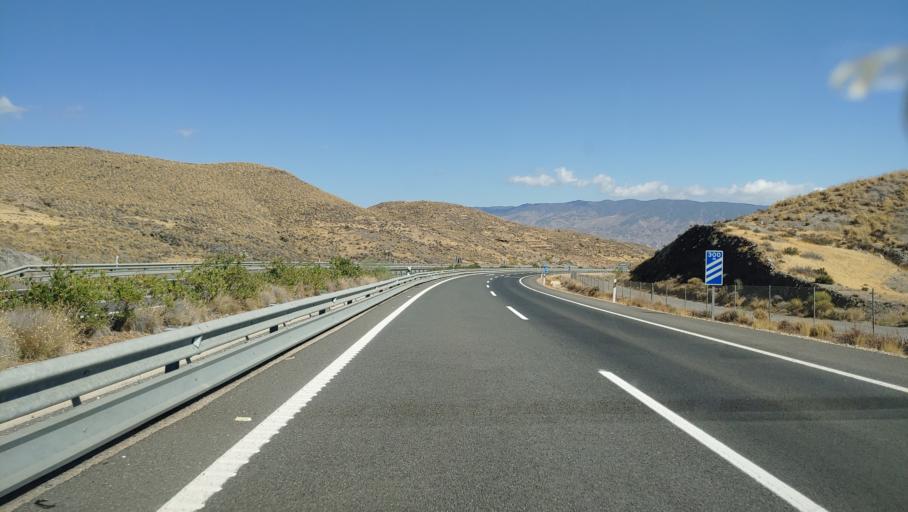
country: ES
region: Andalusia
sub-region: Provincia de Almeria
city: Gergal
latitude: 37.0713
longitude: -2.4957
